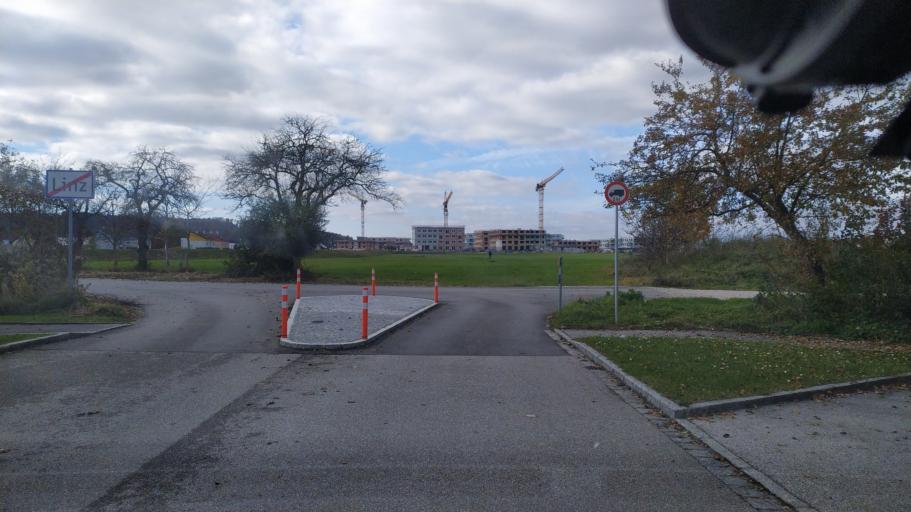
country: AT
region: Upper Austria
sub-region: Politischer Bezirk Urfahr-Umgebung
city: Steyregg
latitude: 48.2544
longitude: 14.3756
